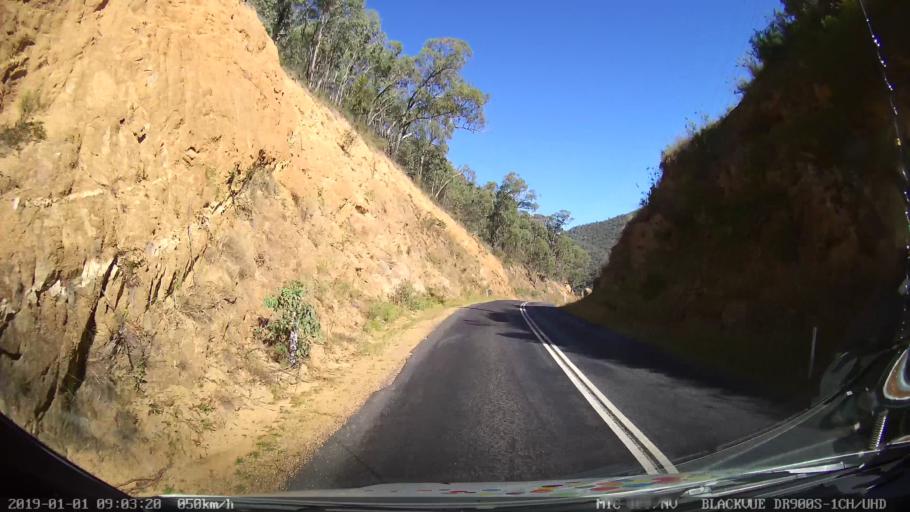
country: AU
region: New South Wales
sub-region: Snowy River
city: Jindabyne
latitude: -36.2242
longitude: 148.1652
